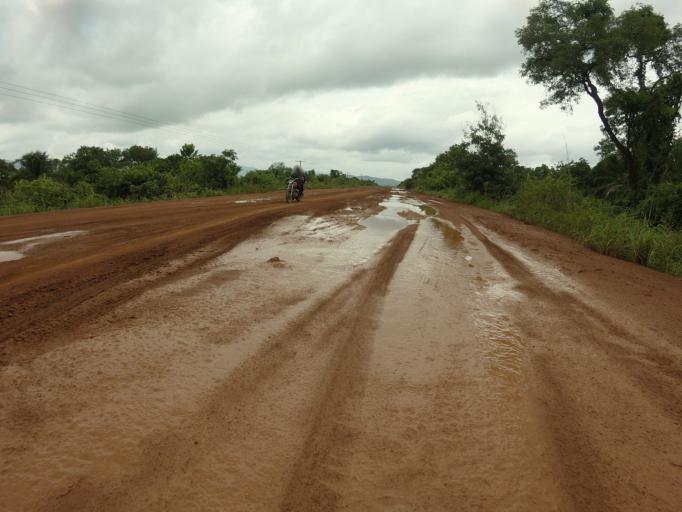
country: GH
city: Kpandae
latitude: 8.3081
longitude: 0.4841
